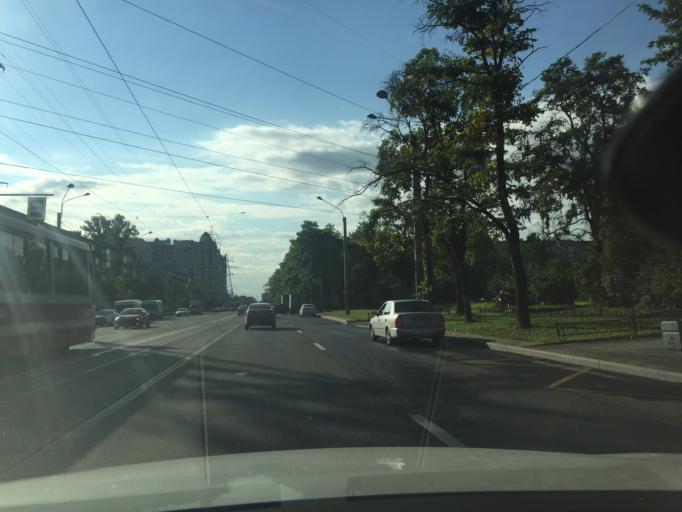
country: RU
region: St.-Petersburg
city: Kupchino
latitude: 59.8359
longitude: 30.3433
